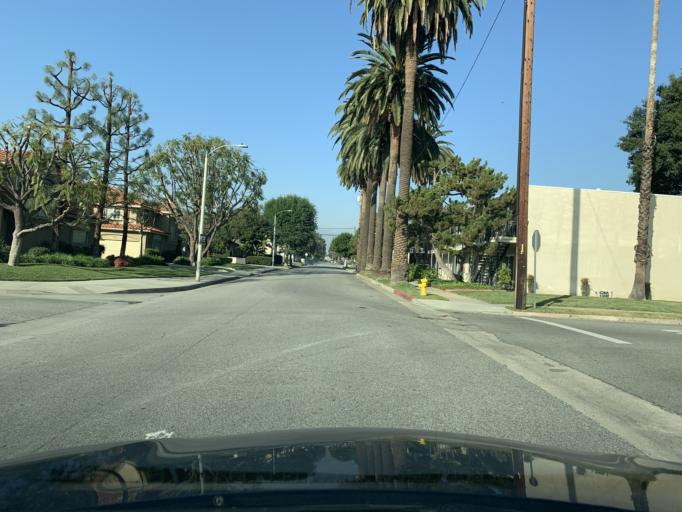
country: US
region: California
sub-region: Los Angeles County
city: Covina
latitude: 34.0838
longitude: -117.8945
